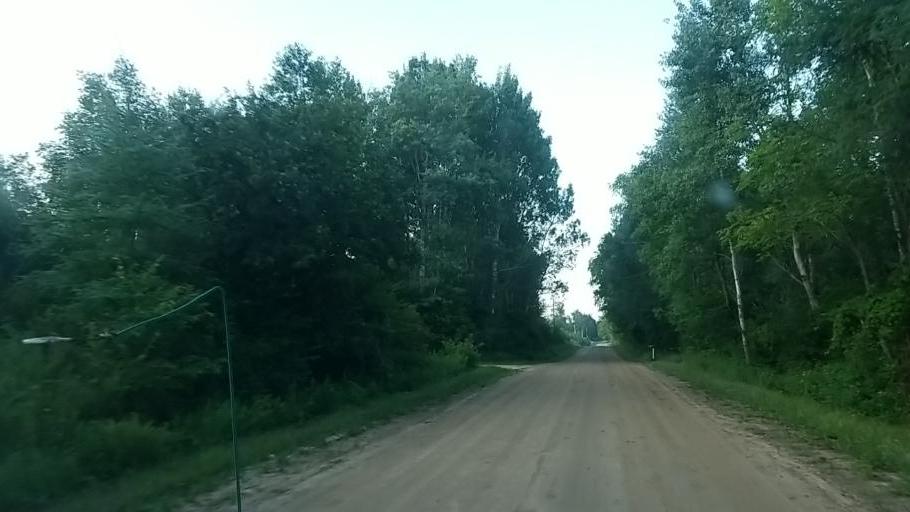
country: US
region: Michigan
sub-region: Osceola County
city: Evart
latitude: 43.9057
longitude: -85.1678
